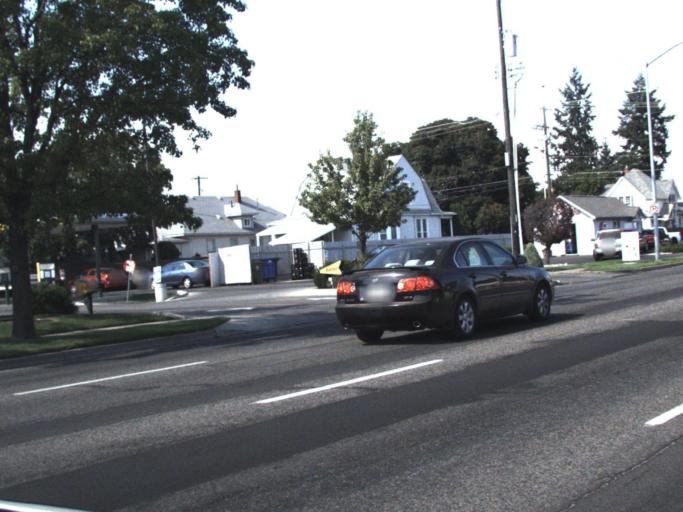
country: US
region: Washington
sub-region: Spokane County
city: Spokane
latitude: 47.6698
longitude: -117.4095
